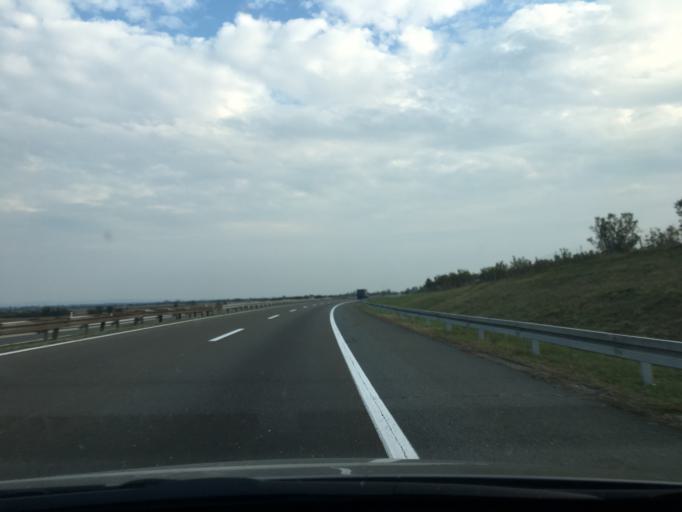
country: RS
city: Lugavcina
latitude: 44.4555
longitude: 21.0431
